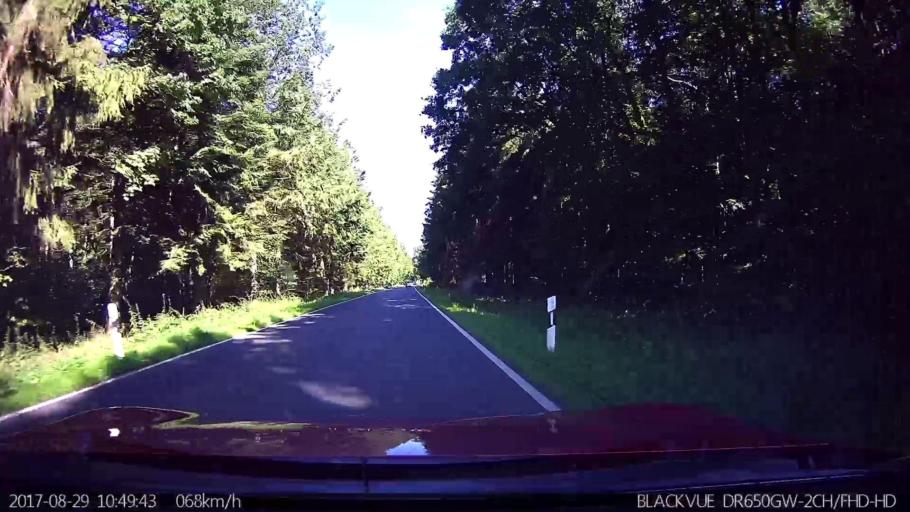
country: DE
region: Mecklenburg-Vorpommern
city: Velgast
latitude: 54.2521
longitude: 12.8234
